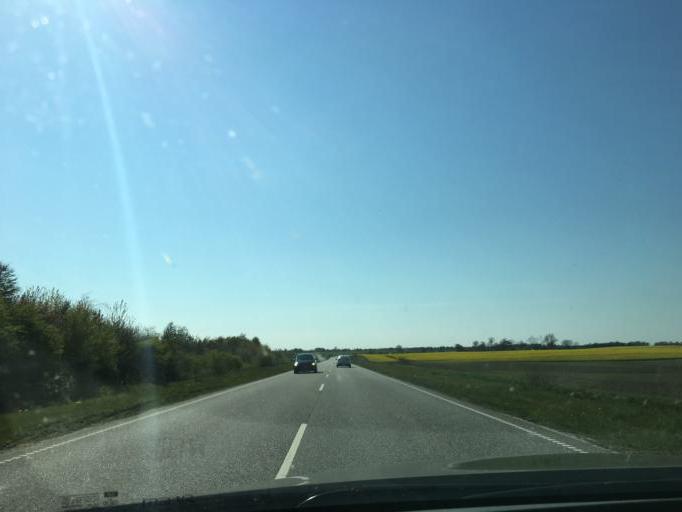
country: DK
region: South Denmark
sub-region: Kolding Kommune
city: Kolding
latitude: 55.5471
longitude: 9.4633
